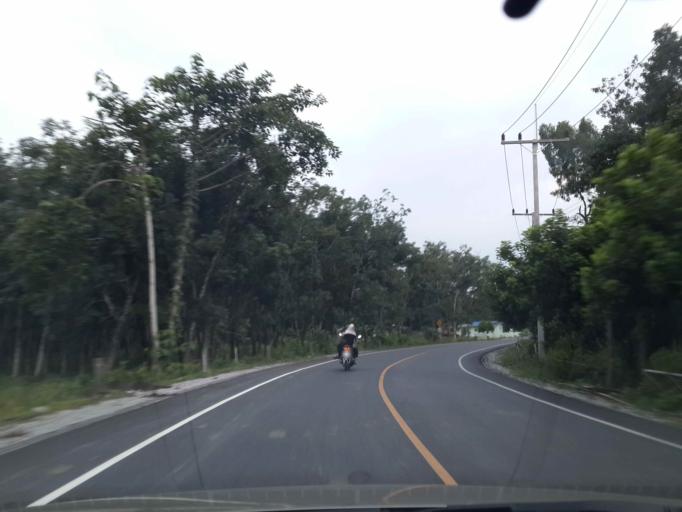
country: TH
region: Narathiwat
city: Rueso
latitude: 6.3467
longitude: 101.4791
